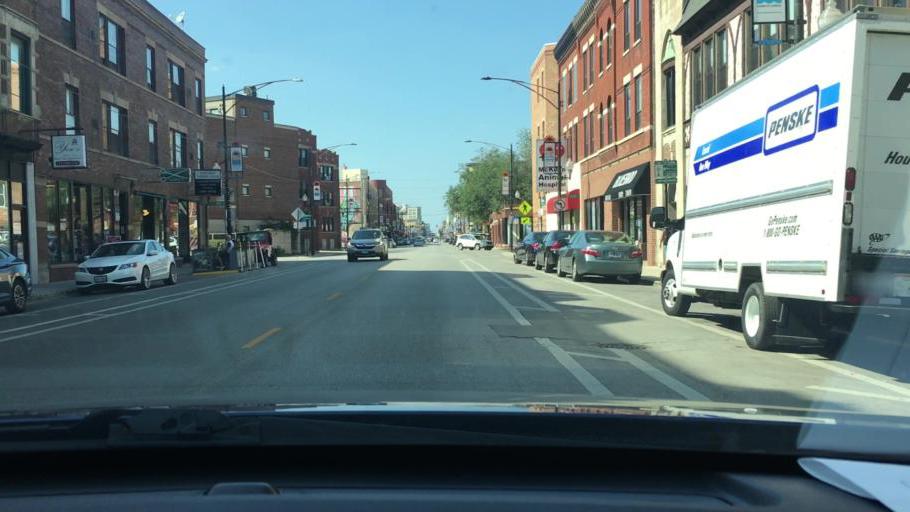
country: US
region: Illinois
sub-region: Cook County
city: Chicago
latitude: 41.9341
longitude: -87.6459
